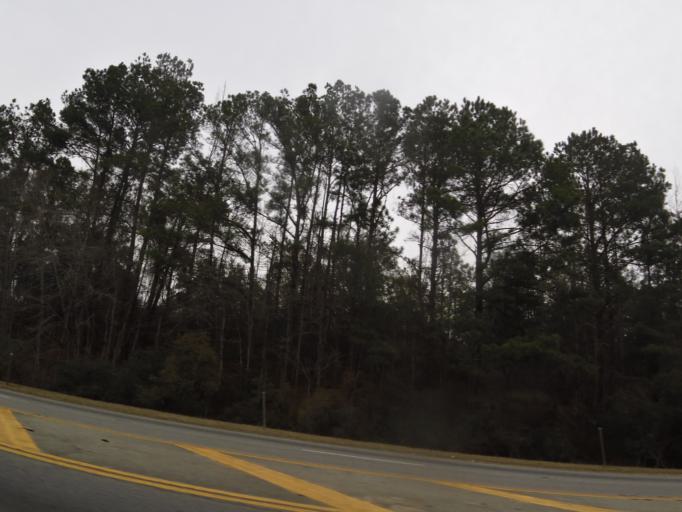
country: US
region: Georgia
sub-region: Thomas County
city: Thomasville
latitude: 30.8721
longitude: -84.0409
